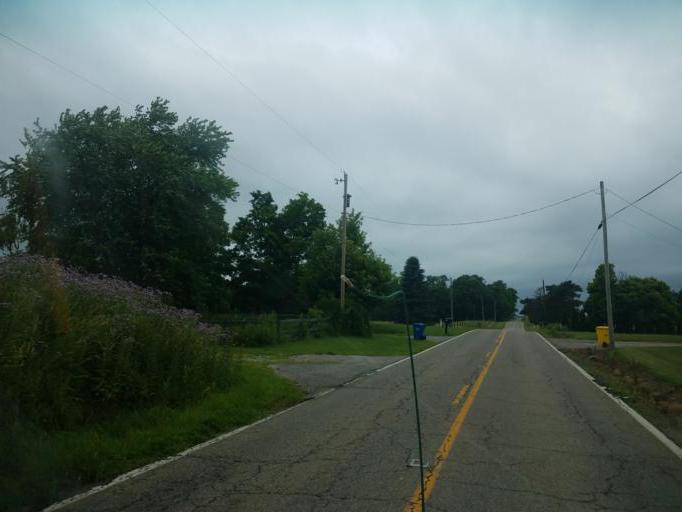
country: US
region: Ohio
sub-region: Columbiana County
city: New Waterford
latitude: 40.8260
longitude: -80.6741
